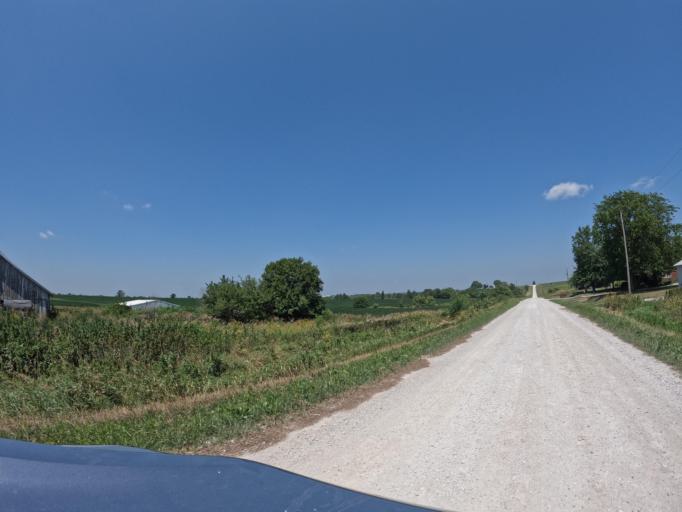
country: US
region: Iowa
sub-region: Keokuk County
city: Sigourney
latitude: 41.2697
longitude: -92.1701
